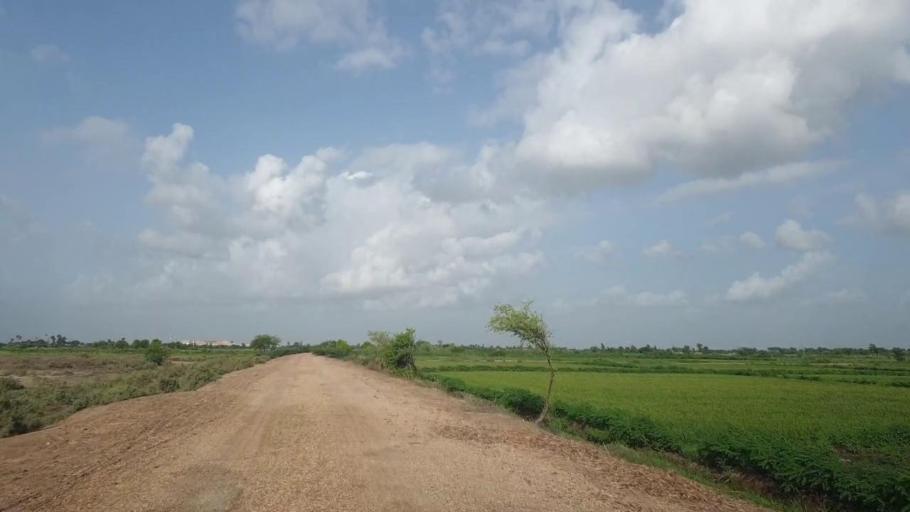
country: PK
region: Sindh
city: Kadhan
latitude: 24.6335
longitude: 69.0900
